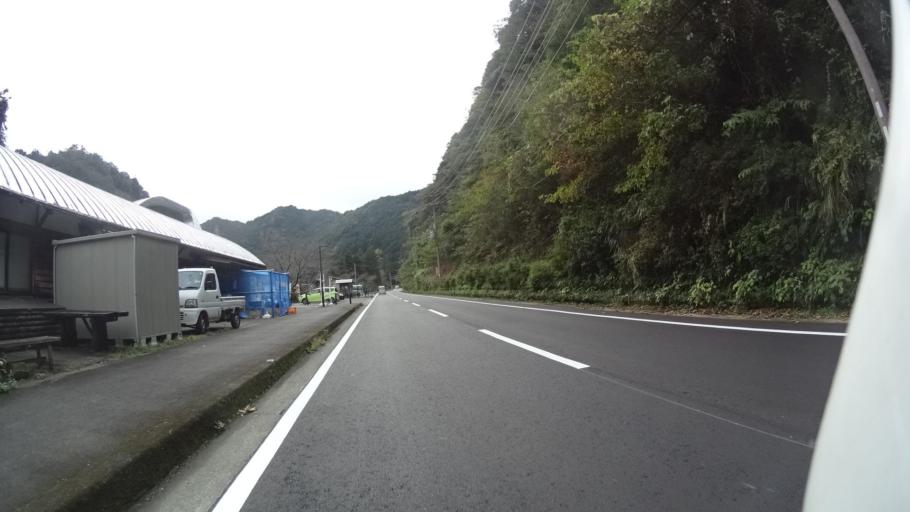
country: JP
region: Wakayama
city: Shingu
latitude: 33.5461
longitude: 135.7198
